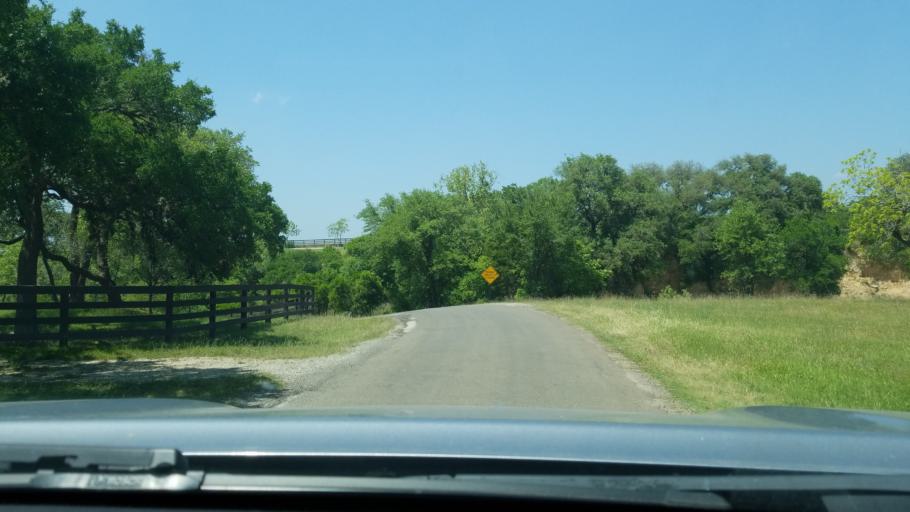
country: US
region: Texas
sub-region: Blanco County
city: Blanco
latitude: 30.0050
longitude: -98.4321
